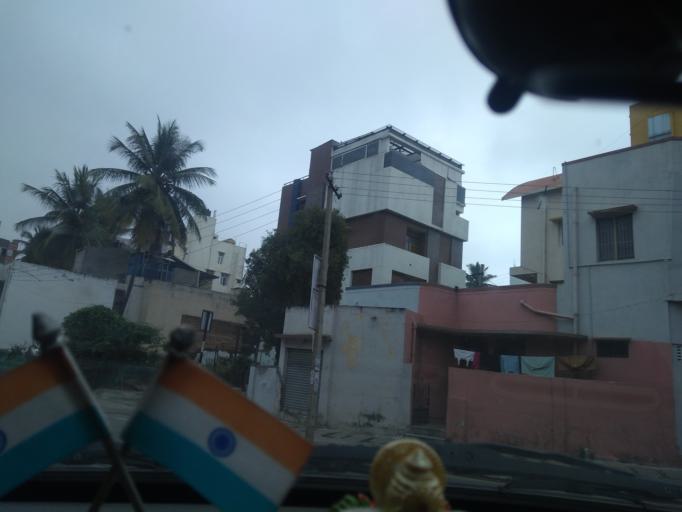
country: IN
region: Karnataka
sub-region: Bangalore Urban
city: Bangalore
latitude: 12.9861
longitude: 77.5510
